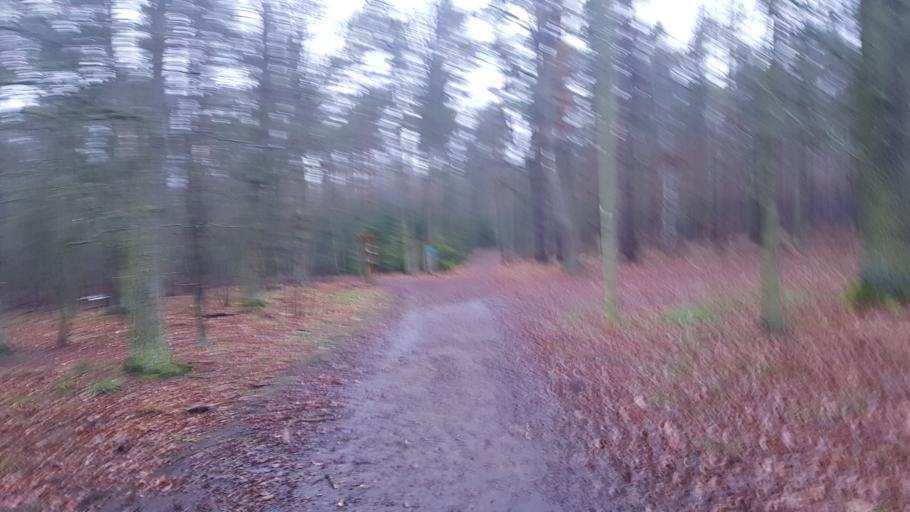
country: DE
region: Brandenburg
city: Stahnsdorf
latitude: 52.3430
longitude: 13.1525
